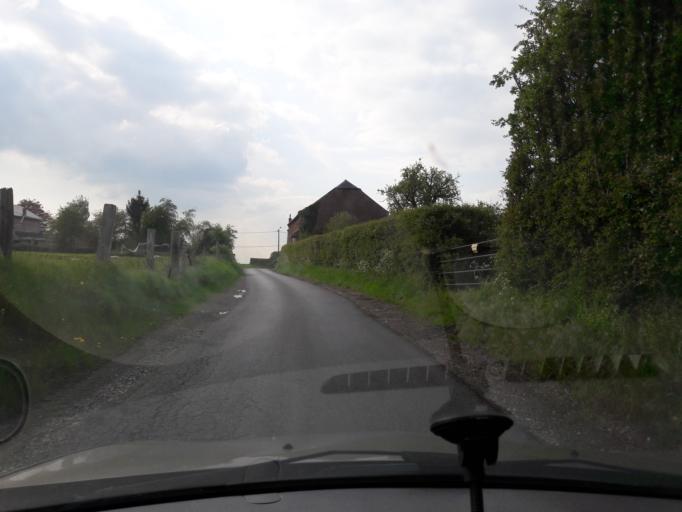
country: FR
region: Nord-Pas-de-Calais
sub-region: Departement du Nord
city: Marpent
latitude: 50.2500
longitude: 4.0726
